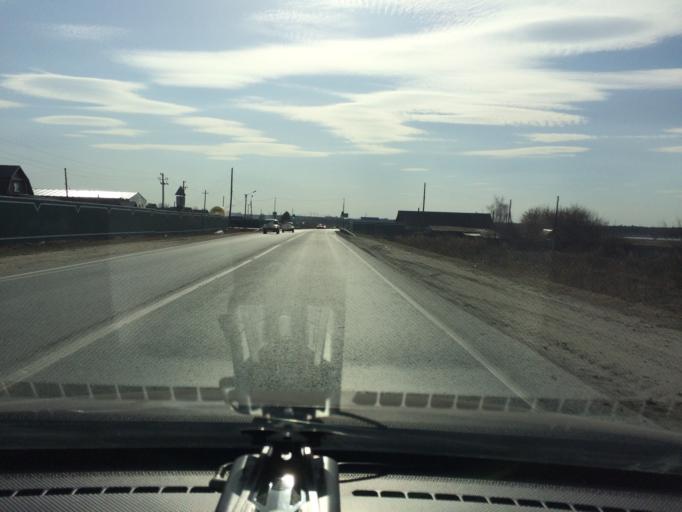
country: RU
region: Mariy-El
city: Yoshkar-Ola
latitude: 56.6600
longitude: 47.9736
